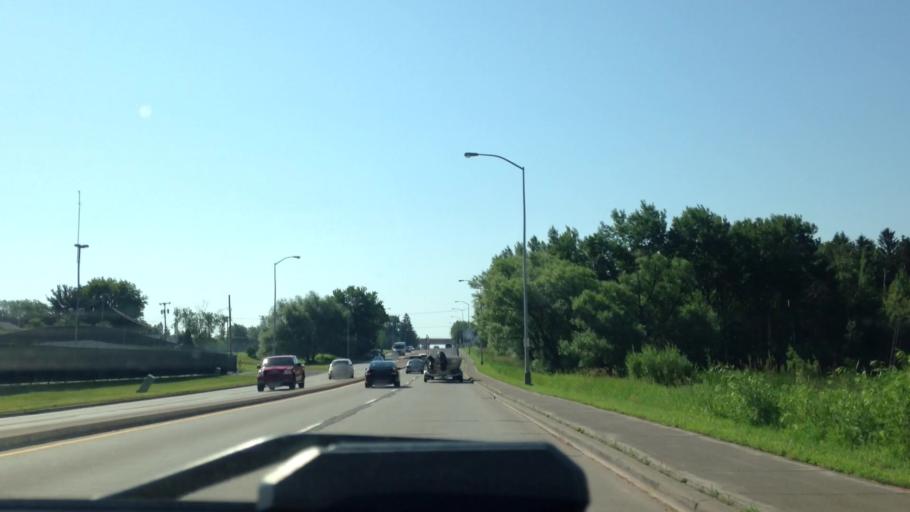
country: US
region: Wisconsin
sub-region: Douglas County
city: Superior
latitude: 46.6939
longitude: -92.0312
